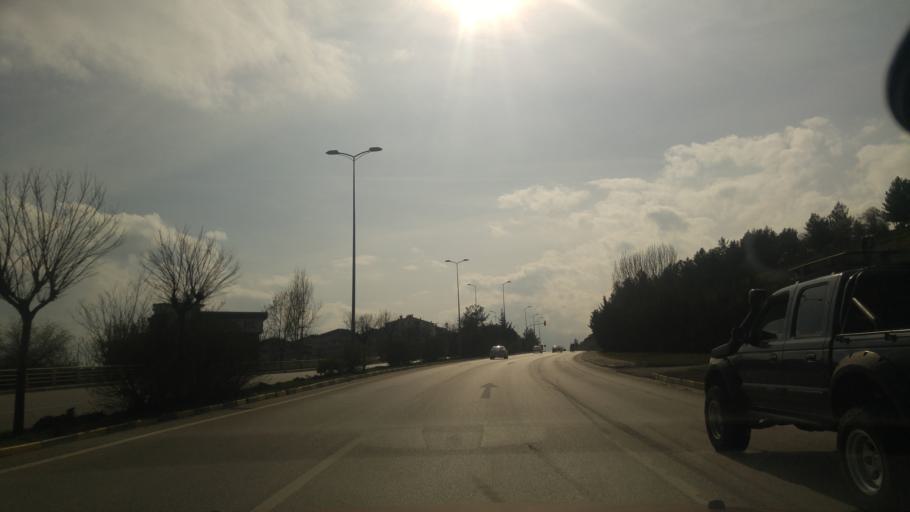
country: TR
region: Karabuk
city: Safranbolu
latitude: 41.2299
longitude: 32.6709
